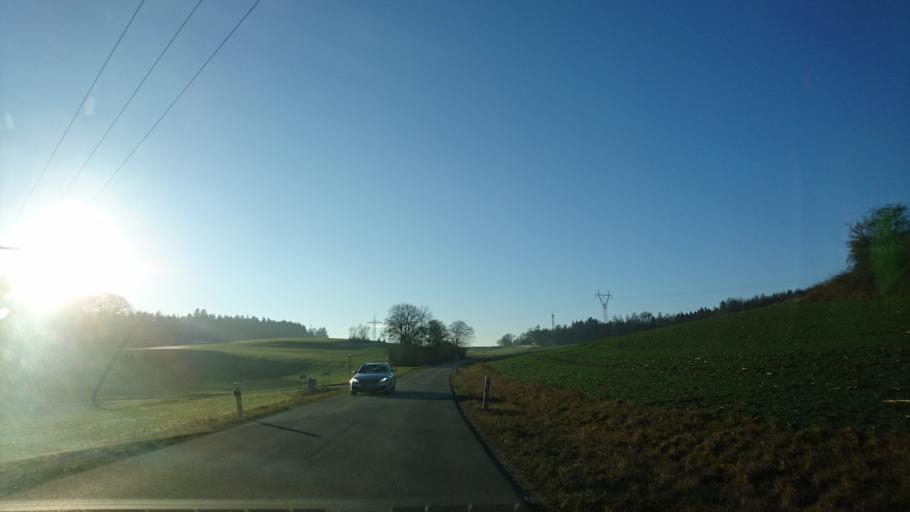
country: DE
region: Bavaria
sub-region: Swabia
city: Adelsried
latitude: 48.4212
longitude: 10.7037
